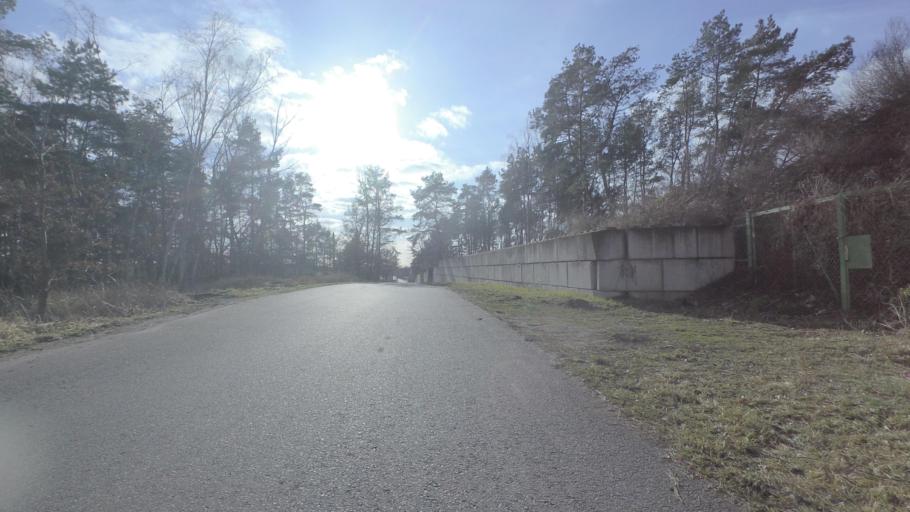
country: DE
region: Brandenburg
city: Trebbin
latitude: 52.2228
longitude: 13.2371
